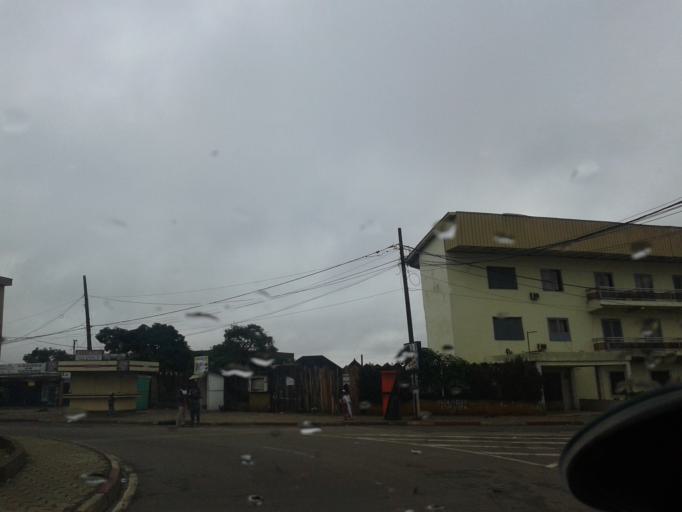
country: CM
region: Centre
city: Yaounde
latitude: 3.8724
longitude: 11.5177
